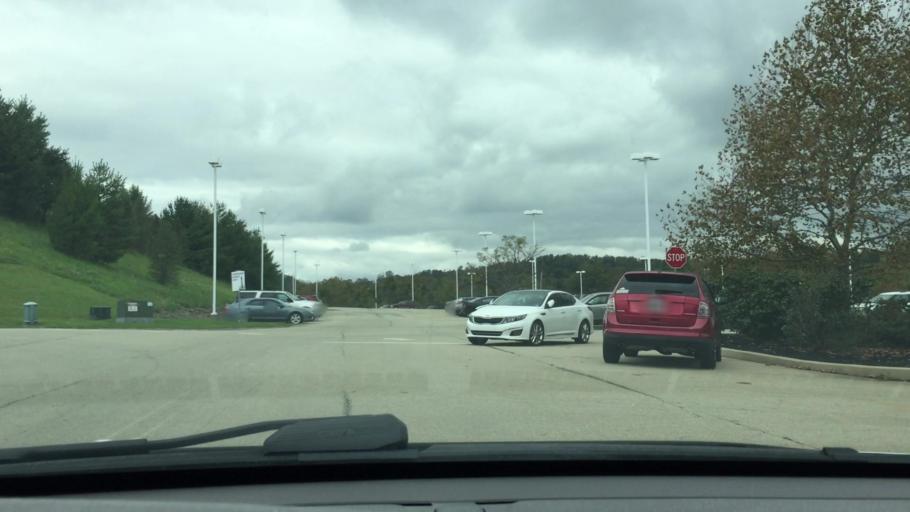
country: US
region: Pennsylvania
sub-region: Westmoreland County
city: Fellsburg
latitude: 40.1629
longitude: -79.7861
